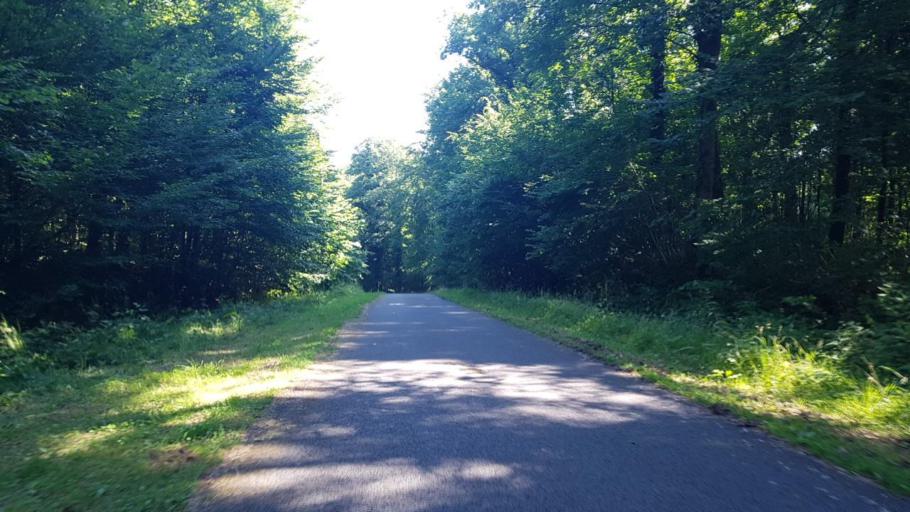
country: FR
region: Picardie
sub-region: Departement de l'Aisne
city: Hirson
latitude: 49.9526
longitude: 4.1050
